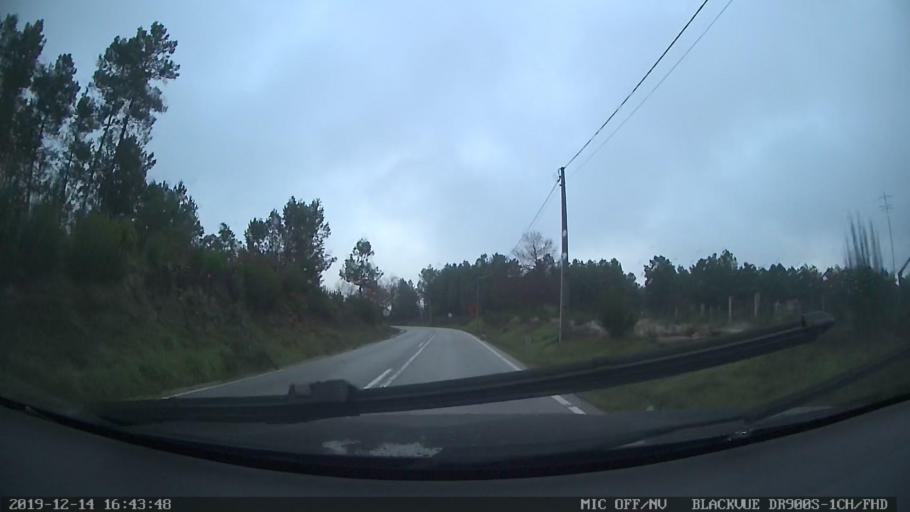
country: PT
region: Vila Real
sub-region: Murca
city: Murca
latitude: 41.3855
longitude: -7.4984
